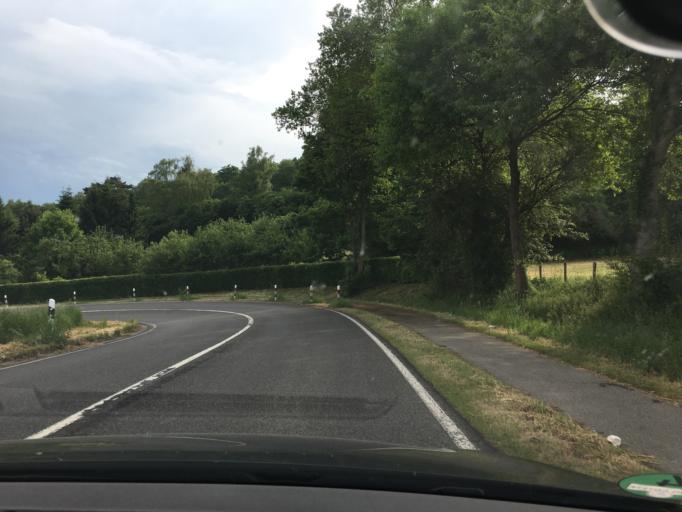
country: DE
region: North Rhine-Westphalia
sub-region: Regierungsbezirk Koln
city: Nideggen
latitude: 50.6830
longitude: 6.4866
